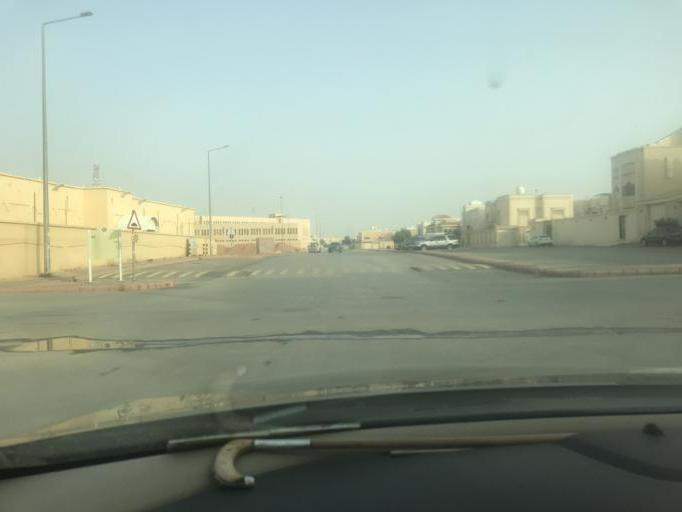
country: SA
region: Ar Riyad
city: Riyadh
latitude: 24.7427
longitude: 46.7727
